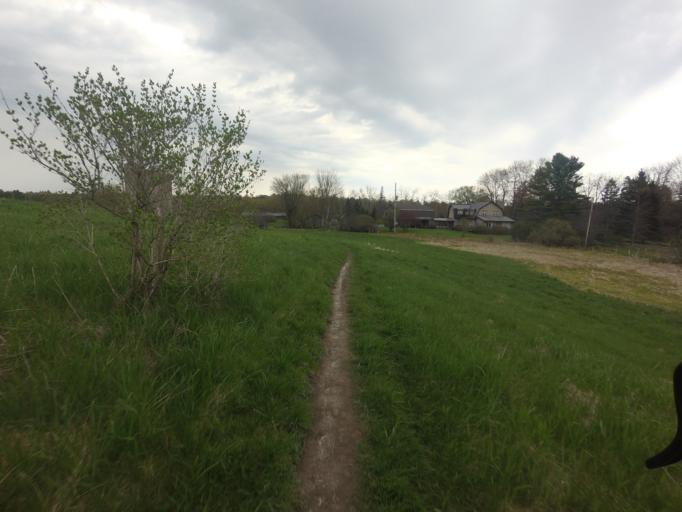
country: CA
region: Ontario
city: Carleton Place
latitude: 45.2281
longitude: -76.2076
